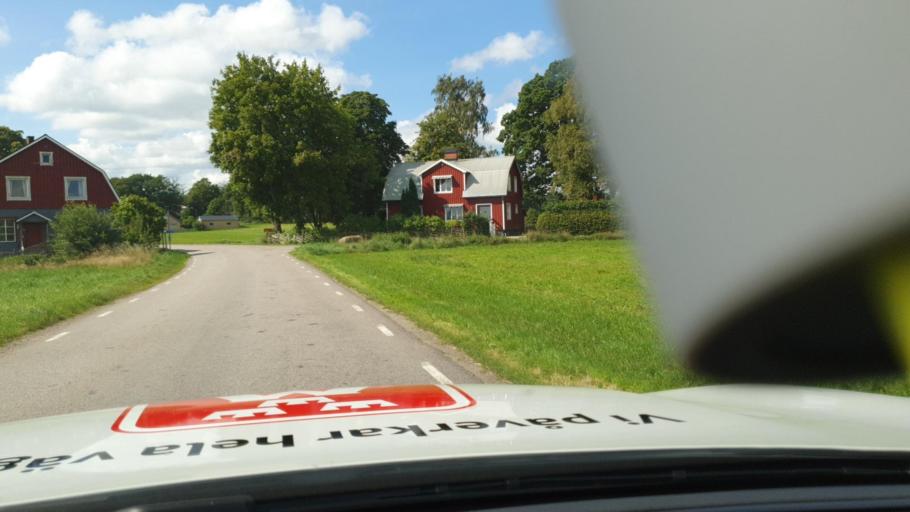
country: SE
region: Halland
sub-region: Laholms Kommun
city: Knared
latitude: 56.4785
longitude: 13.2550
